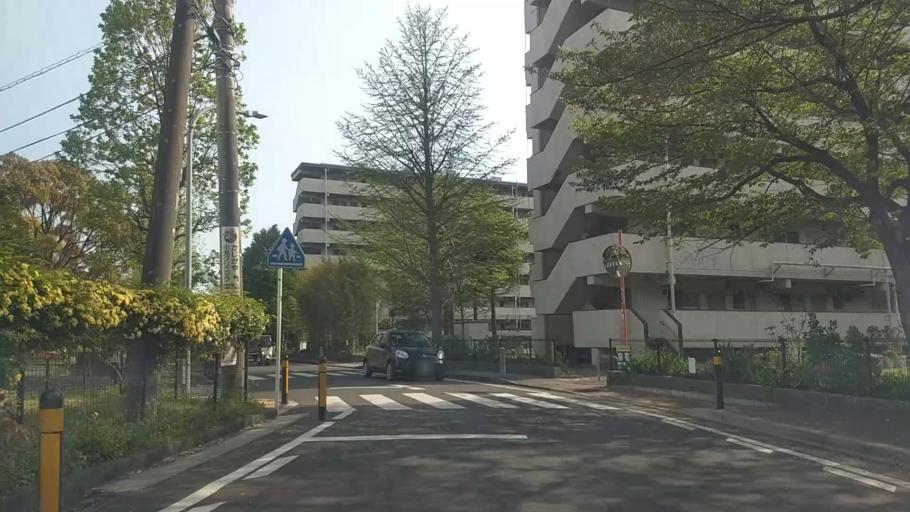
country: JP
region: Kanagawa
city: Kamakura
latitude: 35.3675
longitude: 139.5539
